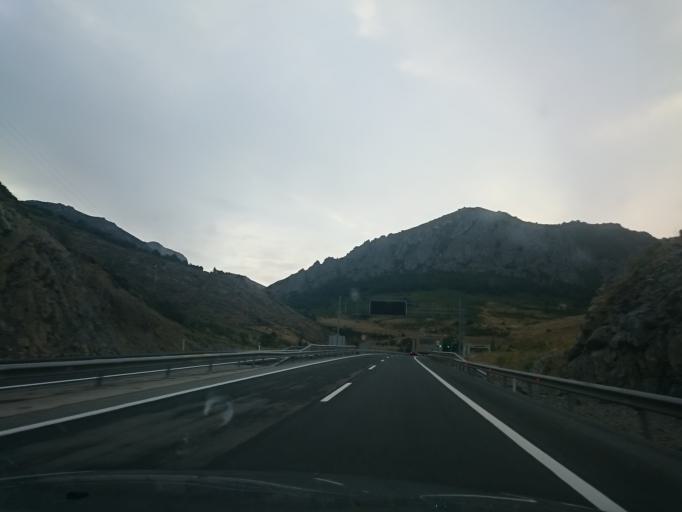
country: ES
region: Castille and Leon
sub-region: Provincia de Leon
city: Sena de Luna
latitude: 42.9383
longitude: -5.8454
